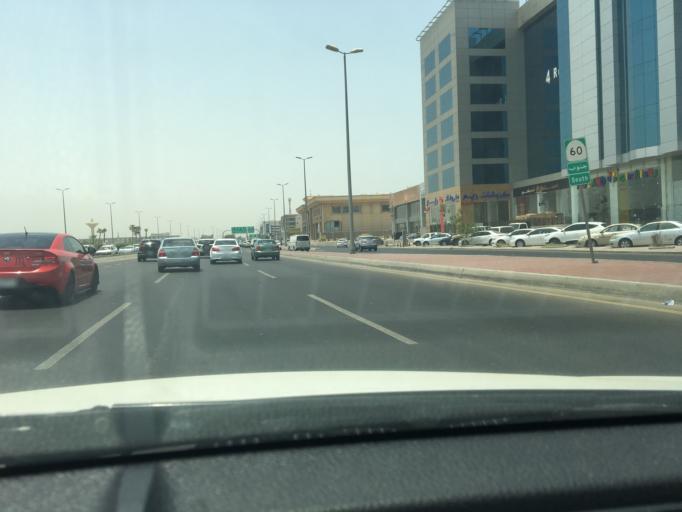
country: SA
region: Makkah
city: Jeddah
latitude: 21.5834
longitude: 39.1771
